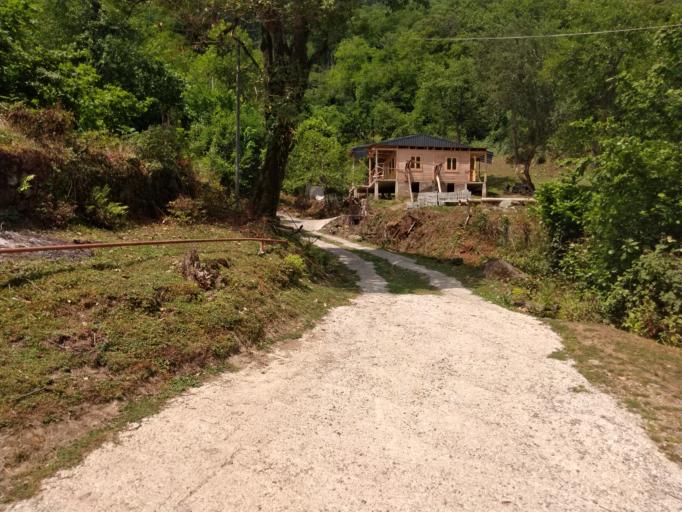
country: TR
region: Artvin
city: Muratli
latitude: 41.5285
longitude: 41.7129
